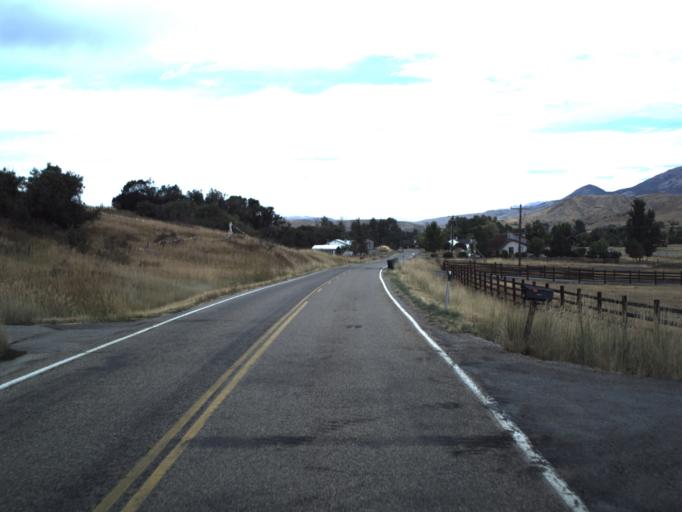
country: US
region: Utah
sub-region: Morgan County
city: Morgan
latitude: 40.9574
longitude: -111.6666
